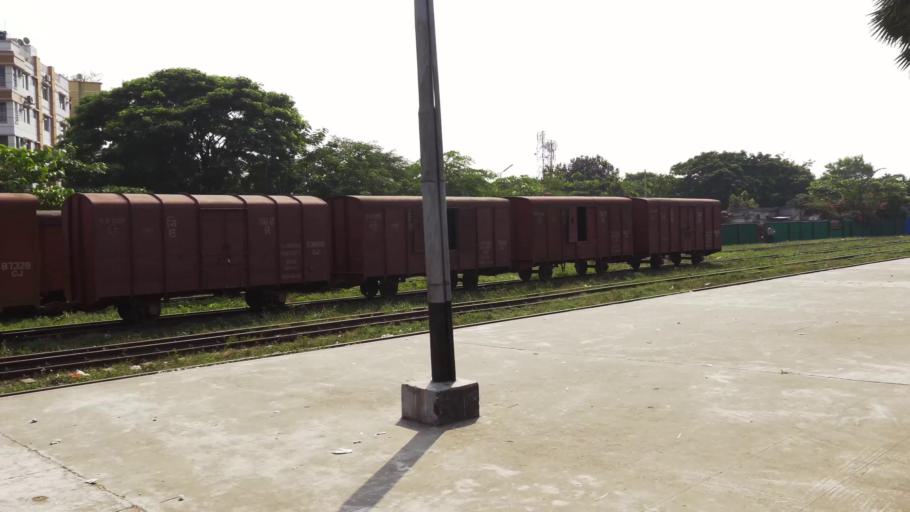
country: BD
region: Dhaka
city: Tungi
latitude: 23.8648
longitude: 90.4061
